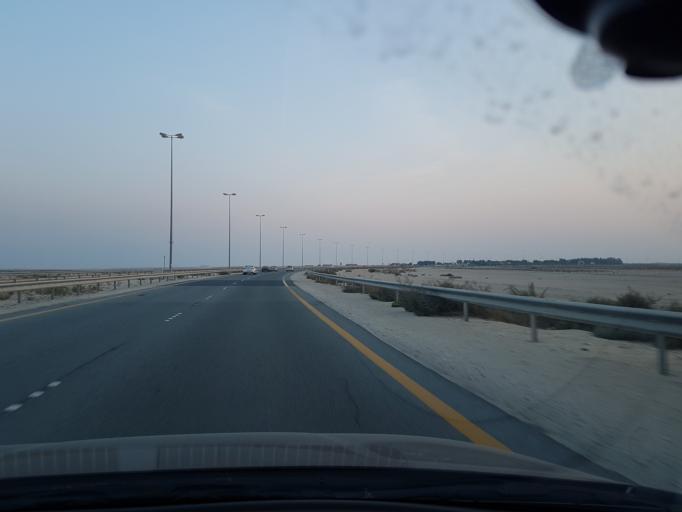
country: BH
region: Central Governorate
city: Dar Kulayb
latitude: 26.0007
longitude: 50.4851
